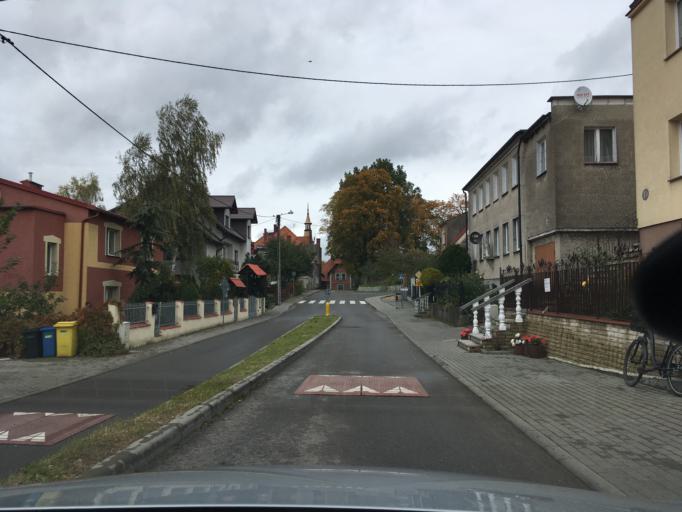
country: PL
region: Pomeranian Voivodeship
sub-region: Powiat koscierski
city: Koscierzyna
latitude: 54.1216
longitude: 17.9878
